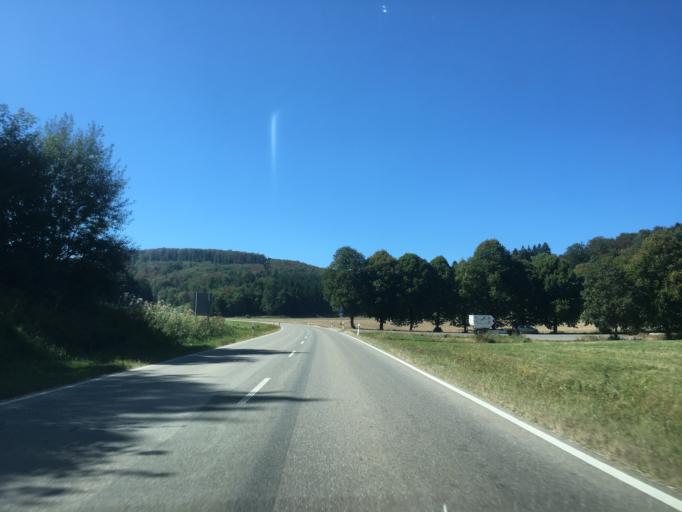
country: DE
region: Baden-Wuerttemberg
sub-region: Tuebingen Region
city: Pfullingen
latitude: 48.4007
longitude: 9.2453
